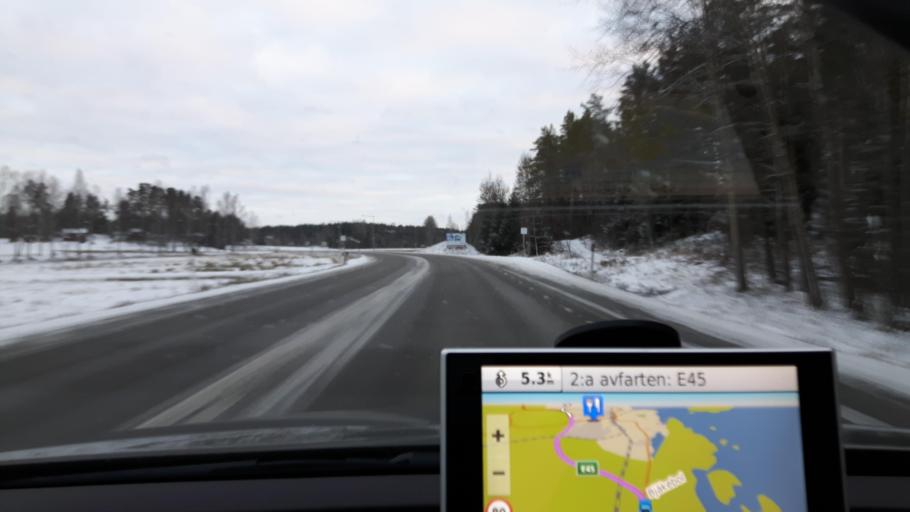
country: SE
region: Vaestra Goetaland
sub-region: Amals Kommun
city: Amal
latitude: 59.0115
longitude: 12.6908
